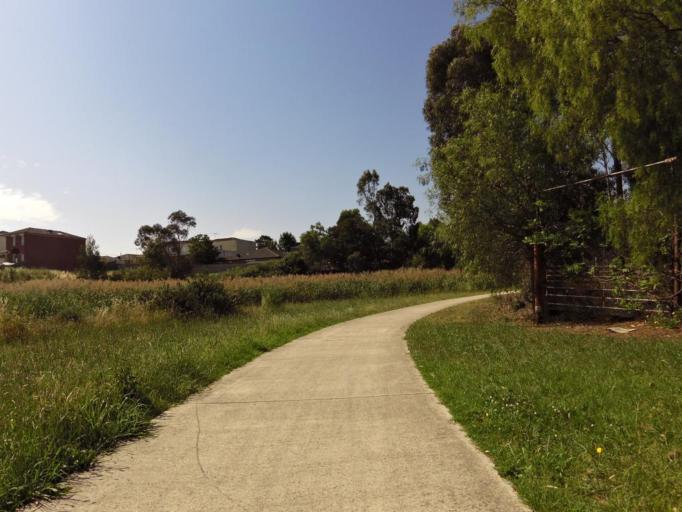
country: AU
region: Victoria
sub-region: Whittlesea
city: Epping
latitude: -37.6508
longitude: 145.0339
